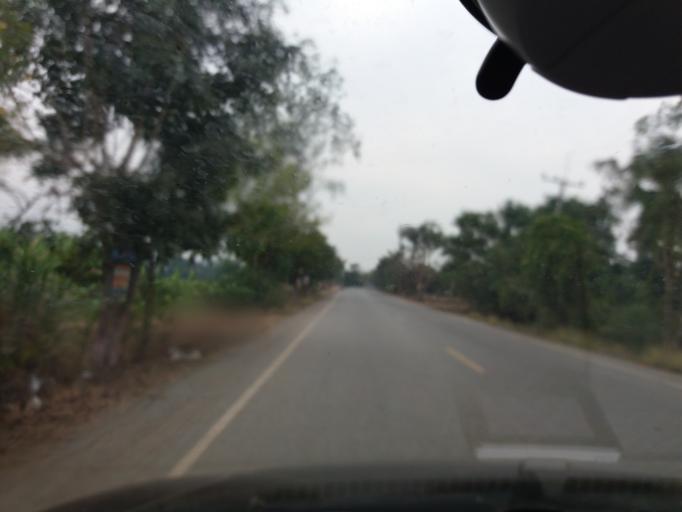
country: TH
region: Suphan Buri
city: Doembang Nangbuat
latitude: 14.8373
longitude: 100.1295
